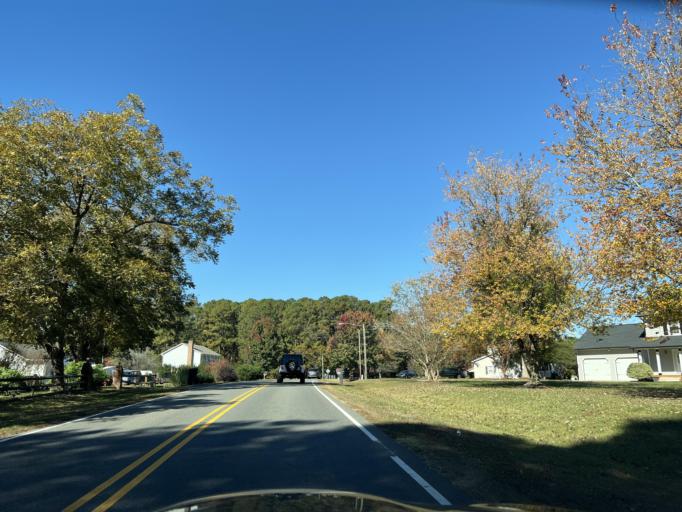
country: US
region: North Carolina
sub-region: Wake County
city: Fuquay-Varina
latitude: 35.6208
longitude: -78.7307
